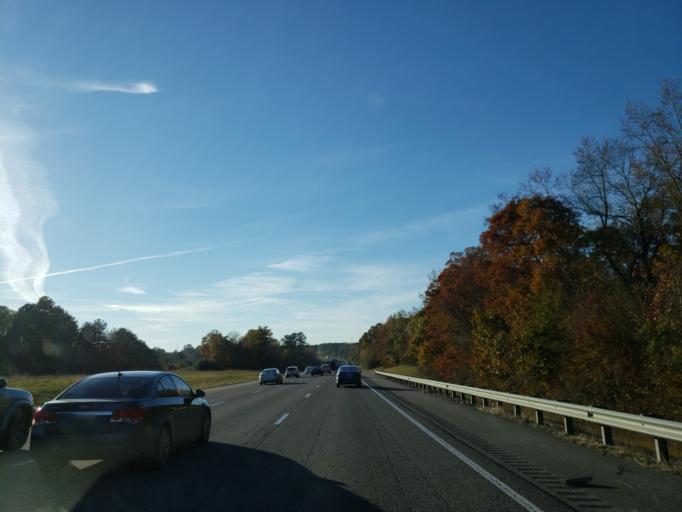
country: US
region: Alabama
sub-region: Tuscaloosa County
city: Coaling
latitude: 33.1840
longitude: -87.3486
